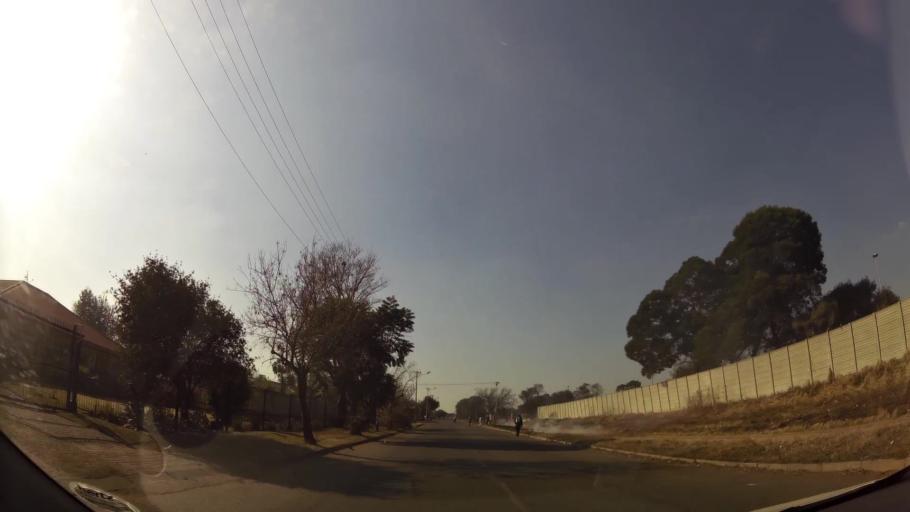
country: ZA
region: Gauteng
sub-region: West Rand District Municipality
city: Randfontein
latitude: -26.1822
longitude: 27.6957
